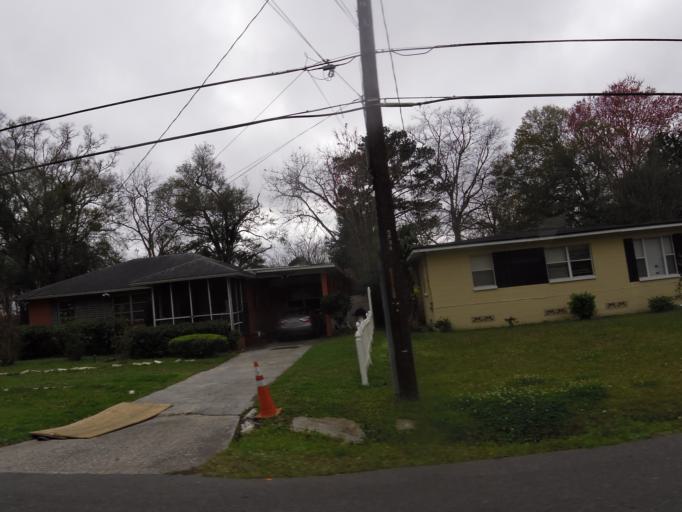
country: US
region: Florida
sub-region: Duval County
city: Jacksonville
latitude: 30.3697
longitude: -81.7126
